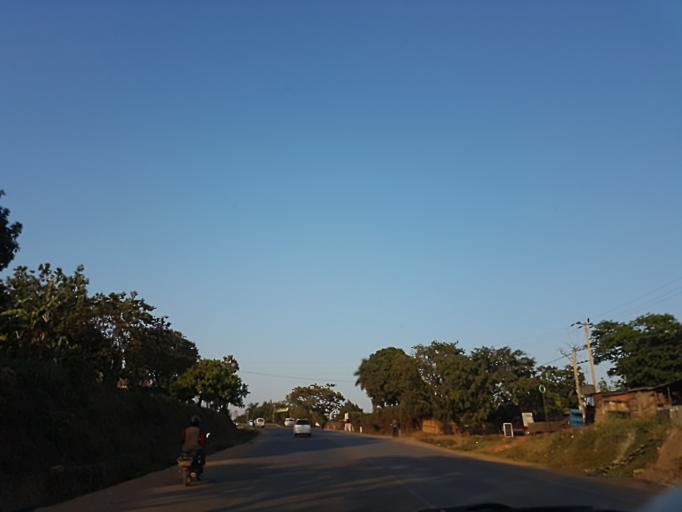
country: UG
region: Central Region
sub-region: Wakiso District
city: Kireka
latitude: 0.4091
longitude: 32.5940
